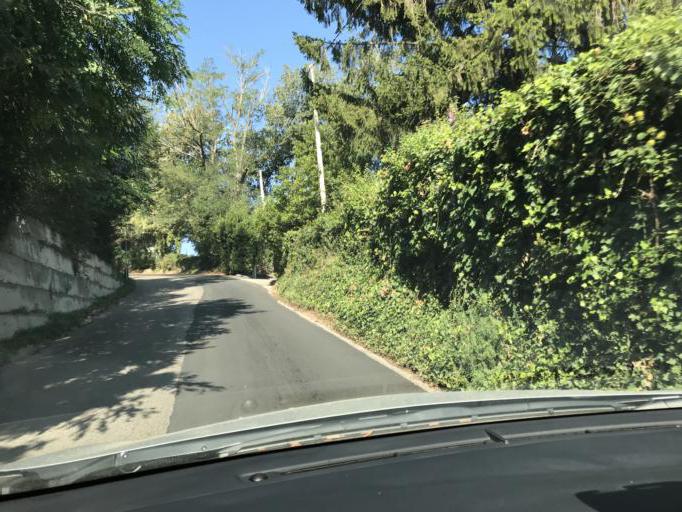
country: IT
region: Umbria
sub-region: Provincia di Perugia
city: Ponte Felcino
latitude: 43.1083
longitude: 12.4419
